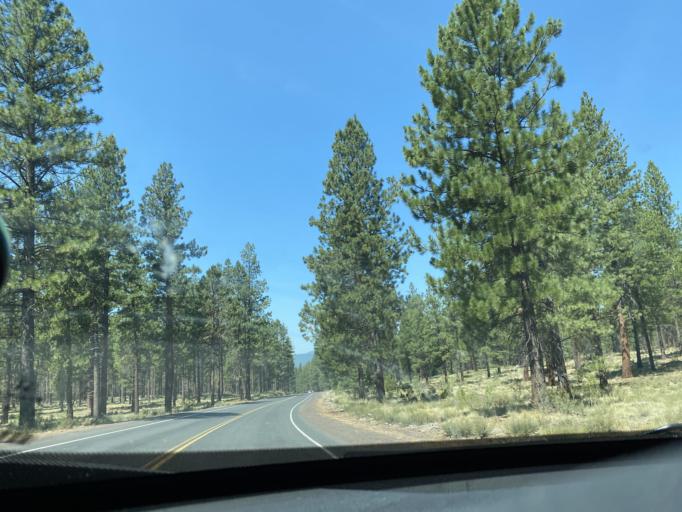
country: US
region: Oregon
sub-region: Deschutes County
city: Sunriver
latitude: 43.8890
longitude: -121.3989
